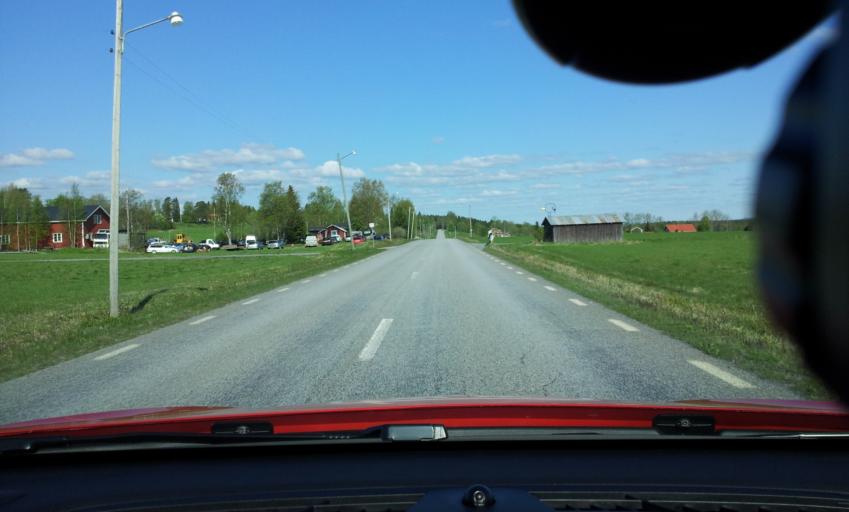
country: SE
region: Jaemtland
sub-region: Krokoms Kommun
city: Krokom
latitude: 63.1446
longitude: 14.1771
